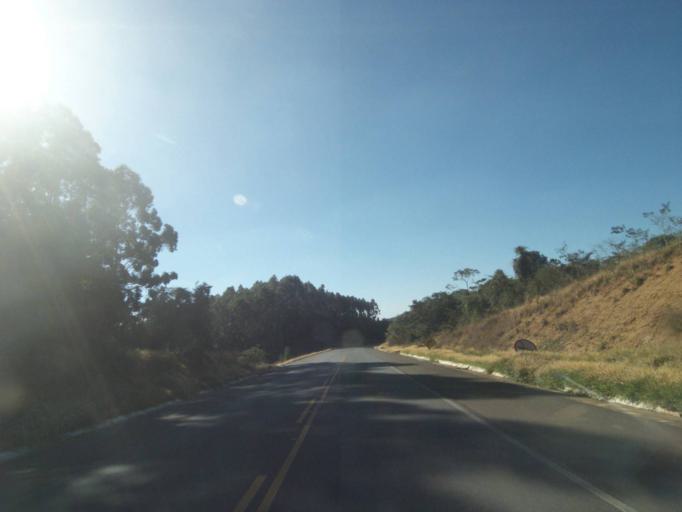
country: BR
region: Parana
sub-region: Tibagi
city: Tibagi
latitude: -24.7515
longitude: -50.4656
